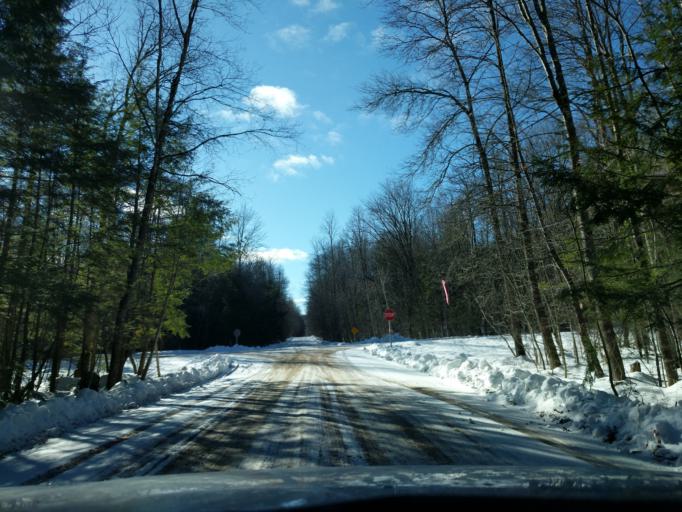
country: US
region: Wisconsin
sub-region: Menominee County
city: Keshena
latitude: 45.0886
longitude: -88.6250
